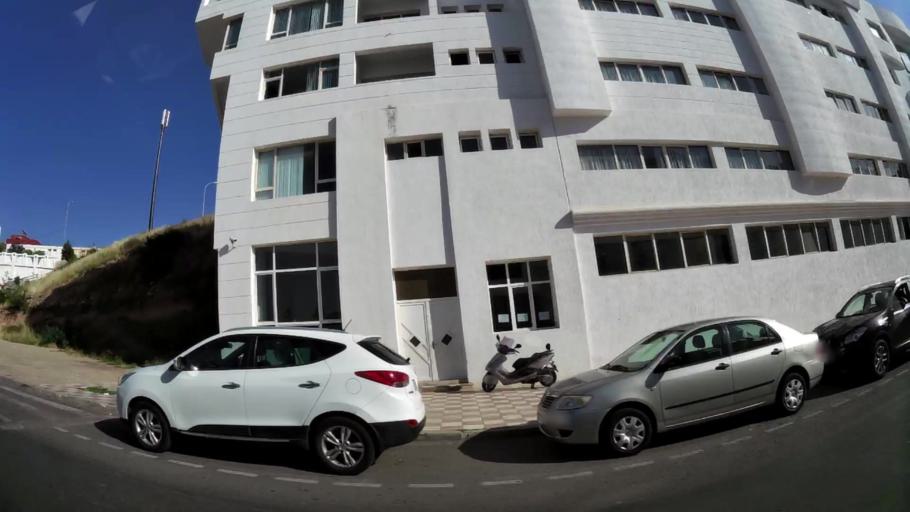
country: MA
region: Souss-Massa-Draa
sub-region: Agadir-Ida-ou-Tnan
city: Agadir
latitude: 30.4314
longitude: -9.5843
